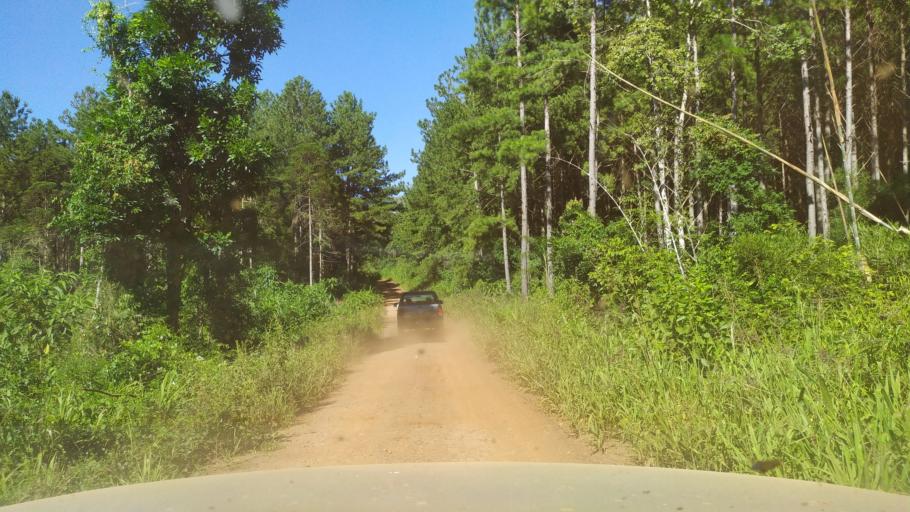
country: AR
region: Misiones
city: Caraguatay
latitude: -26.6748
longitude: -54.6999
